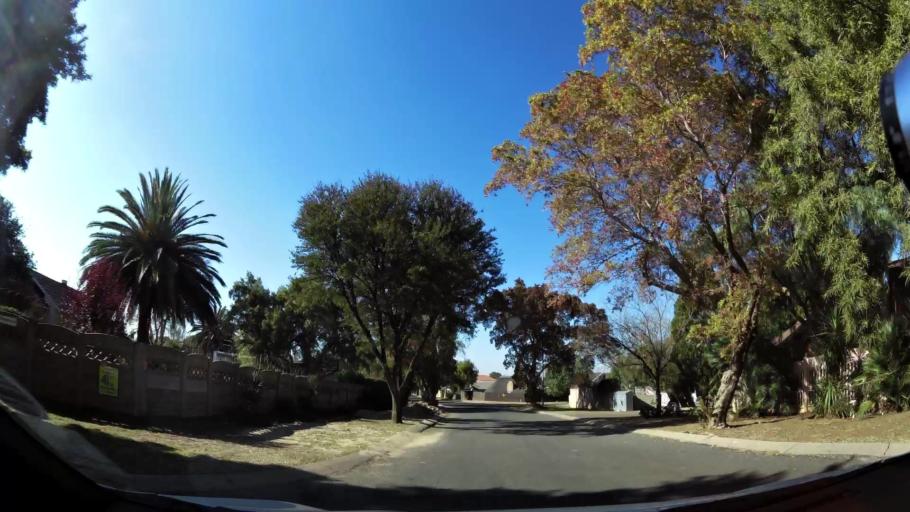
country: ZA
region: Gauteng
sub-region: Ekurhuleni Metropolitan Municipality
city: Germiston
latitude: -26.3293
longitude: 28.1066
